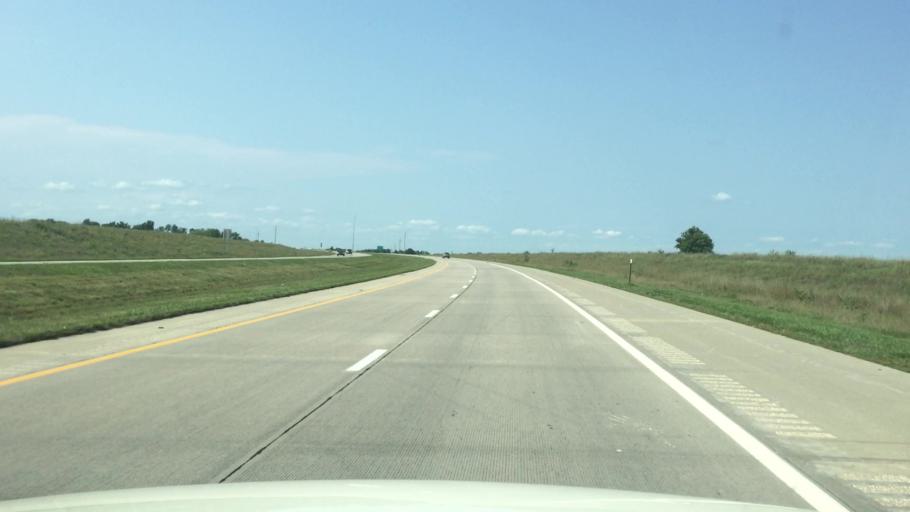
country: US
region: Kansas
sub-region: Linn County
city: Pleasanton
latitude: 38.1727
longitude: -94.6959
